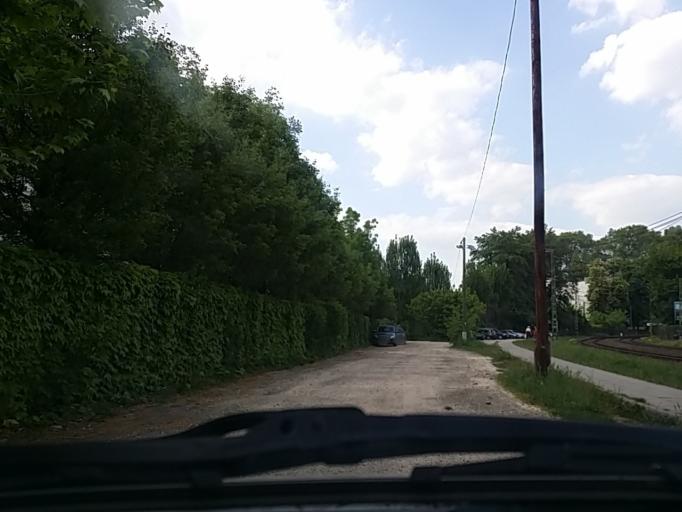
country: HU
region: Pest
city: Urom
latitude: 47.5839
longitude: 19.0443
